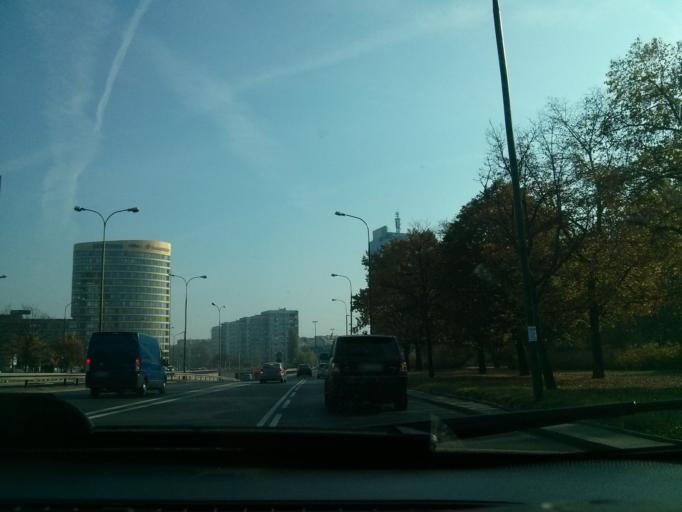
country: PL
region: Masovian Voivodeship
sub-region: Warszawa
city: Warsaw
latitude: 52.2171
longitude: 21.0117
